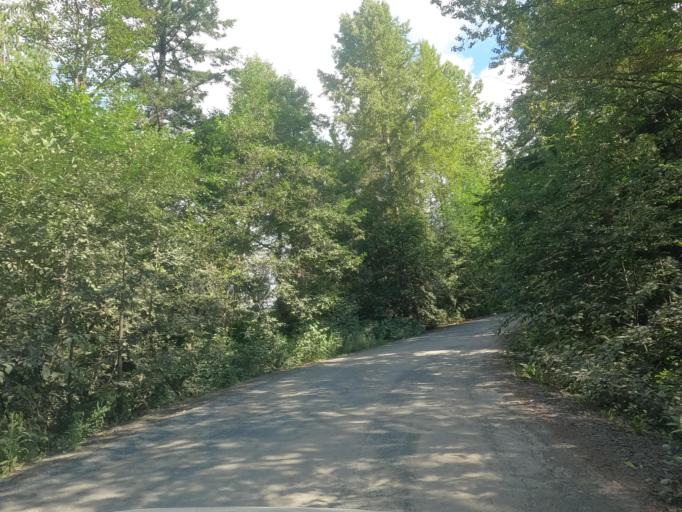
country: CA
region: British Columbia
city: Whistler
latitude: 50.0652
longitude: -123.1000
